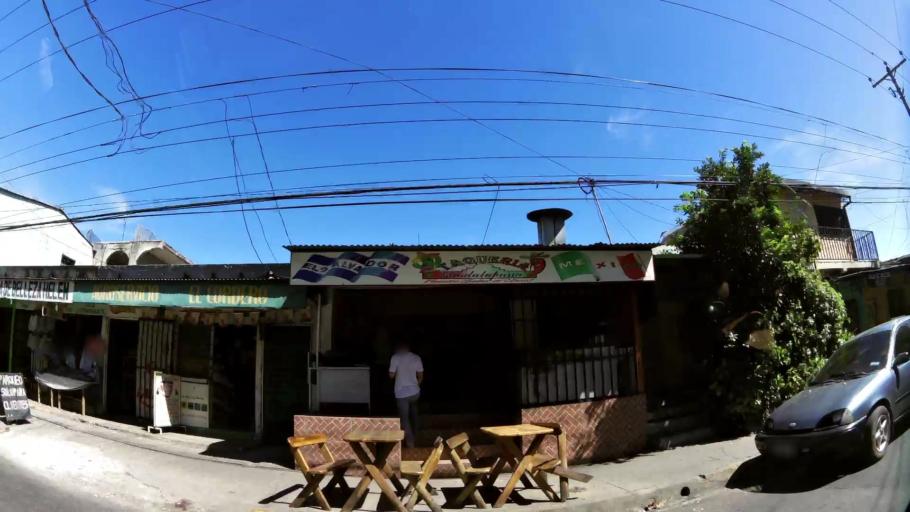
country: SV
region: San Salvador
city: Apopa
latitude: 13.7966
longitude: -89.1780
